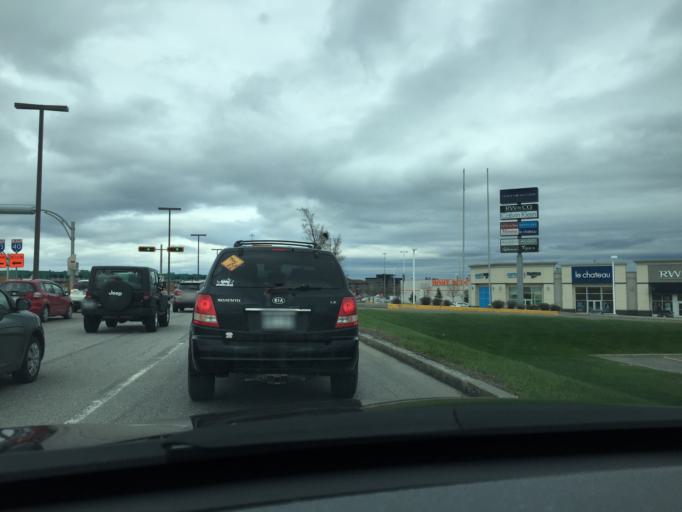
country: CA
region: Quebec
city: Quebec
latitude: 46.8447
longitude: -71.2741
